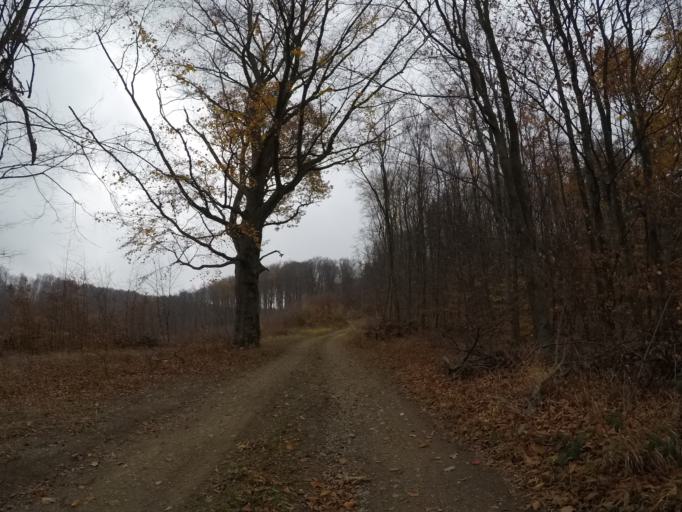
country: SK
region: Presovsky
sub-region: Okres Presov
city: Presov
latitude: 48.8919
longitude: 21.1732
